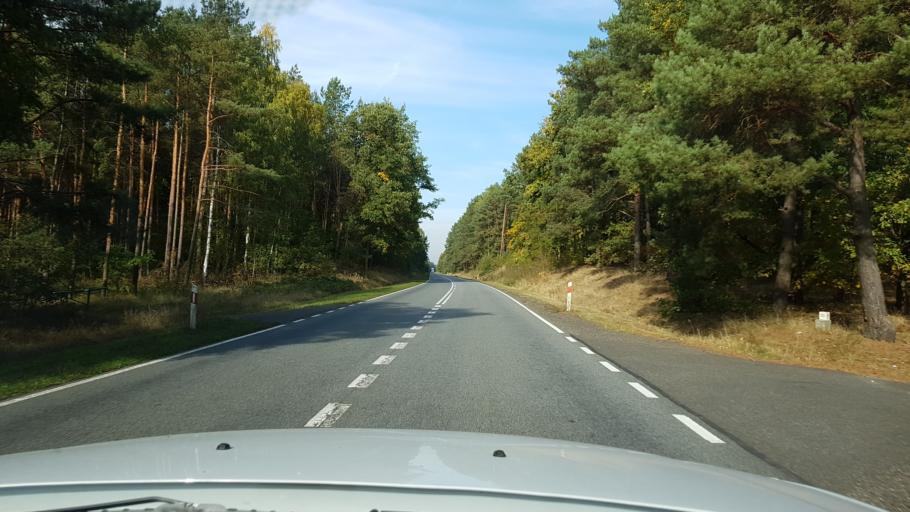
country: PL
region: West Pomeranian Voivodeship
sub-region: Powiat mysliborski
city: Nowogrodek Pomorski
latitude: 52.9184
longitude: 14.9664
